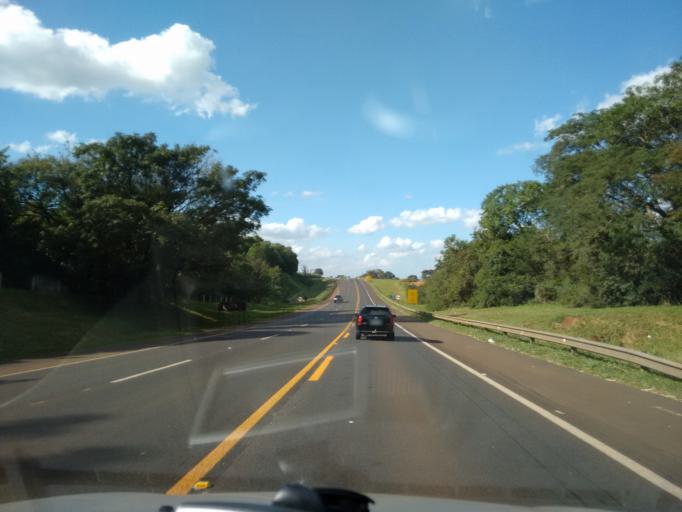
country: BR
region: Sao Paulo
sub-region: Americo Brasiliense
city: Americo Brasiliense
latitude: -21.7580
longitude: -48.0729
